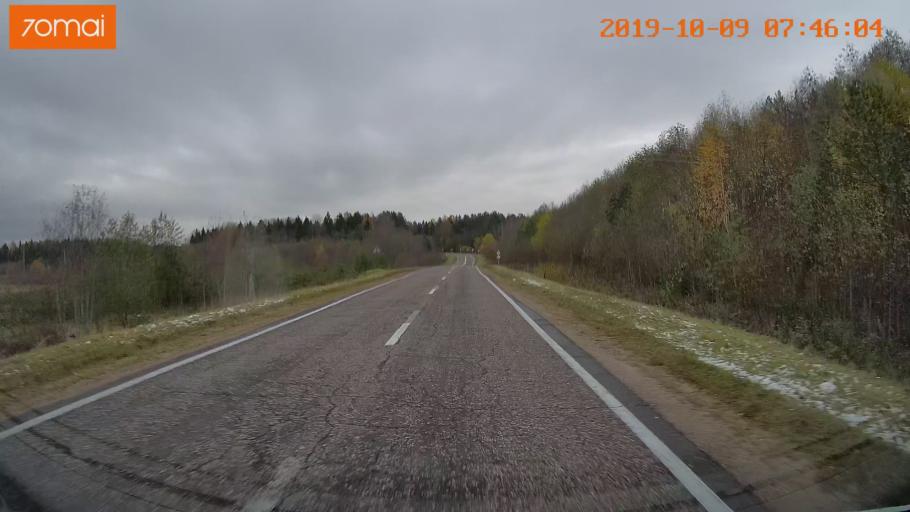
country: RU
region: Jaroslavl
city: Kukoboy
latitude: 58.6559
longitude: 39.7803
